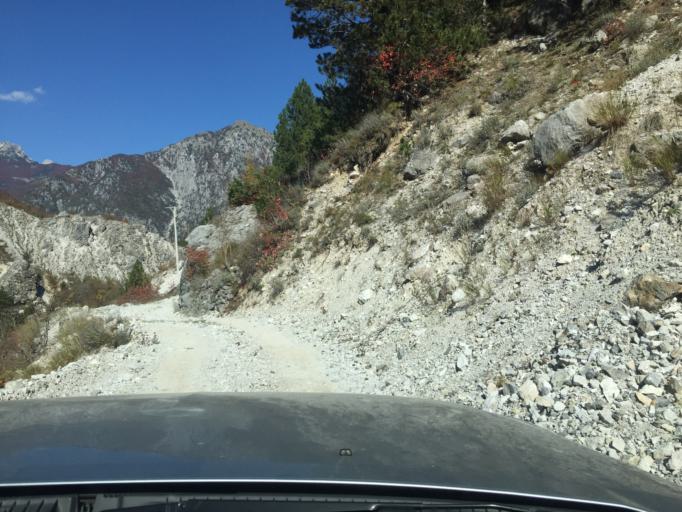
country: AL
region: Shkoder
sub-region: Rrethi i Shkodres
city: Nicaj-Shale
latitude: 42.3323
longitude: 19.7750
